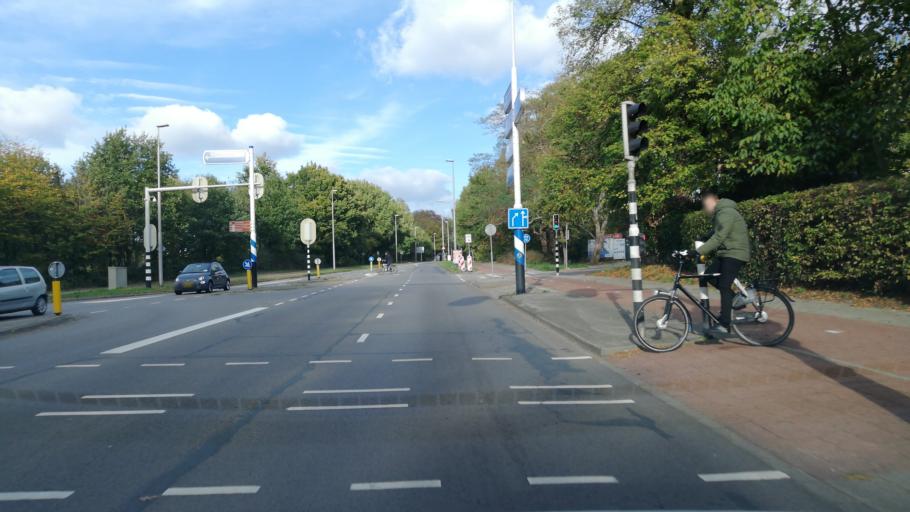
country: NL
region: Gelderland
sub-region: Gemeente Arnhem
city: Arnhem
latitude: 51.9944
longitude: 5.9106
